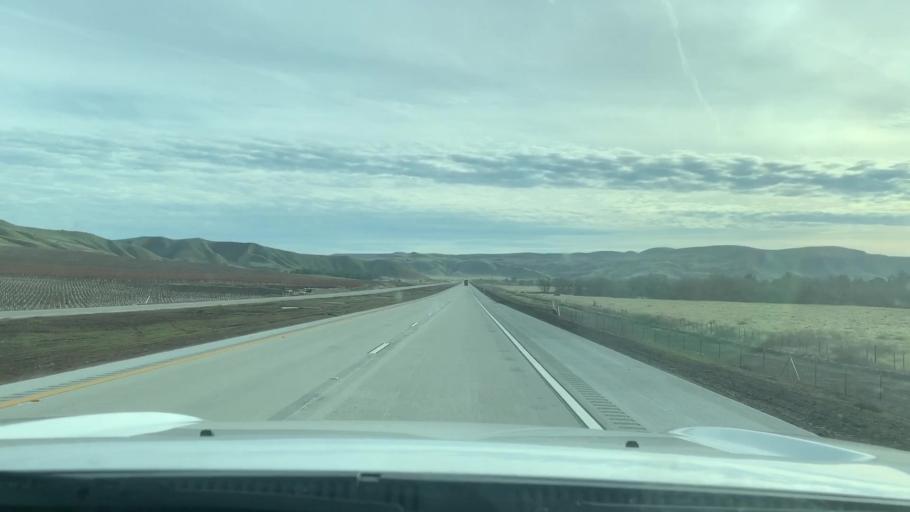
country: US
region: California
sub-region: San Luis Obispo County
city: Shandon
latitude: 35.6624
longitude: -120.3890
